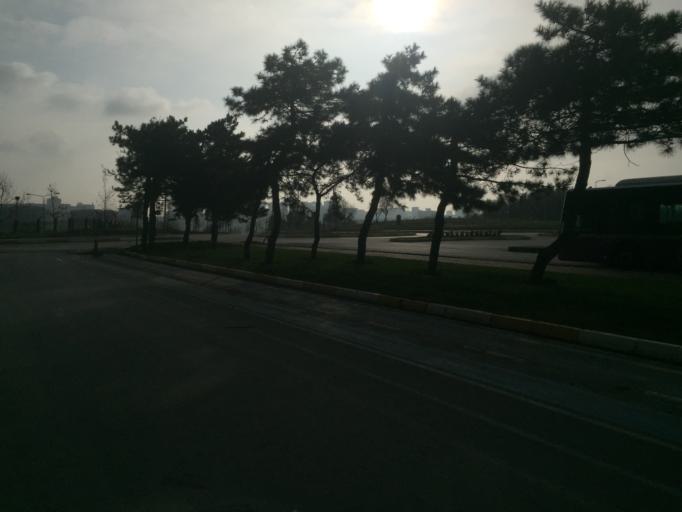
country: TR
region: Istanbul
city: merter keresteciler
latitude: 41.0259
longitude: 28.8936
